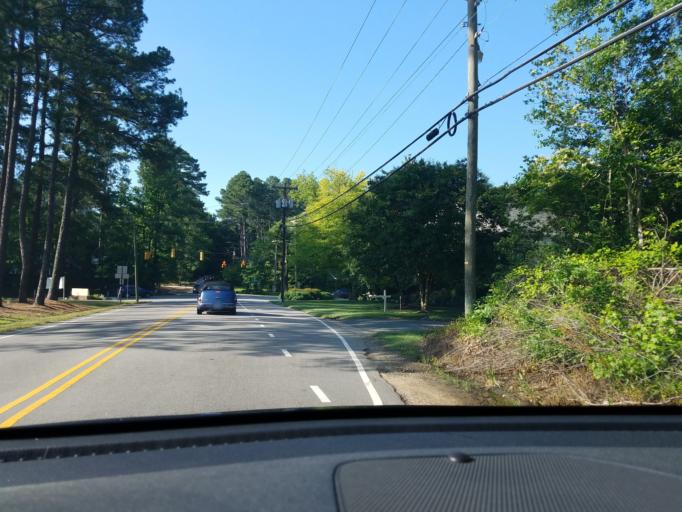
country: US
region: North Carolina
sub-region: Durham County
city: Durham
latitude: 35.9694
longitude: -78.9324
